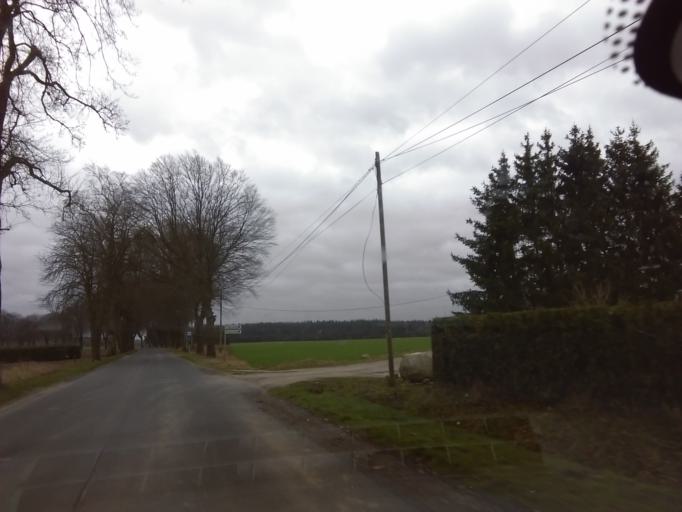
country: PL
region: Greater Poland Voivodeship
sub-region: Powiat zlotowski
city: Lipka
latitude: 53.4712
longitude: 17.2946
